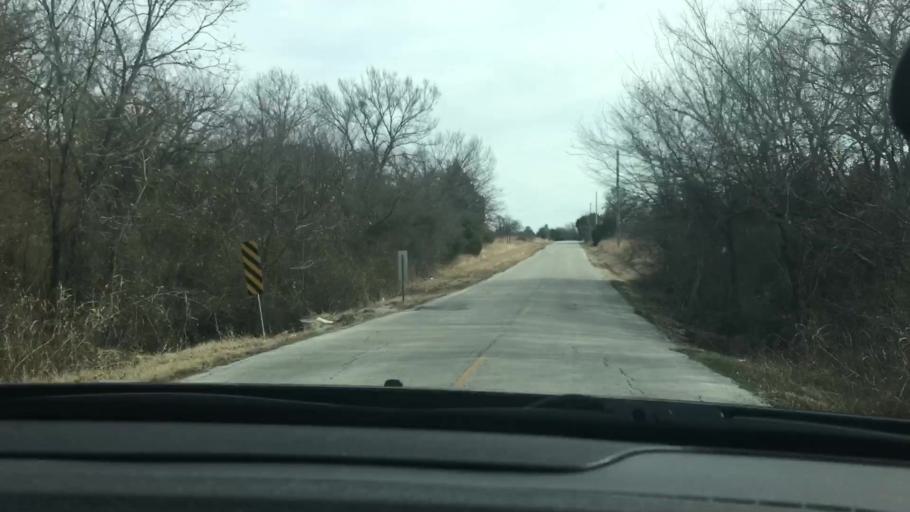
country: US
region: Oklahoma
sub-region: Carter County
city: Ardmore
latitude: 34.1744
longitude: -97.0834
